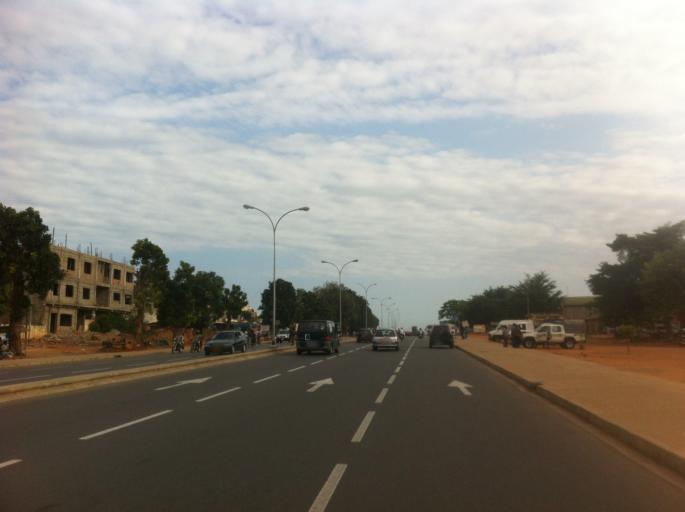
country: TG
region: Maritime
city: Lome
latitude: 6.1573
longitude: 1.2016
